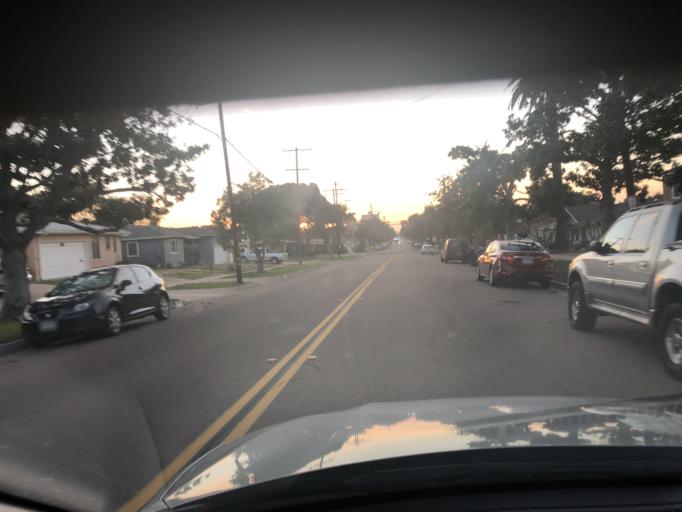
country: US
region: California
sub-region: San Diego County
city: Chula Vista
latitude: 32.6440
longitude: -117.0705
